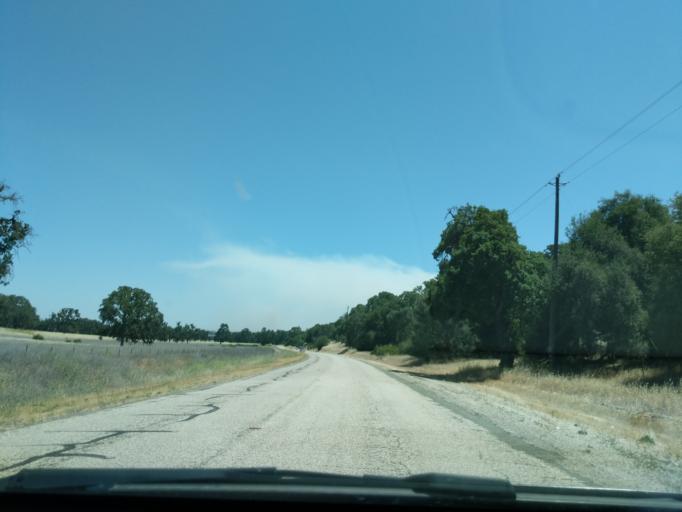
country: US
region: California
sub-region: Monterey County
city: King City
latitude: 36.0449
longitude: -121.1829
